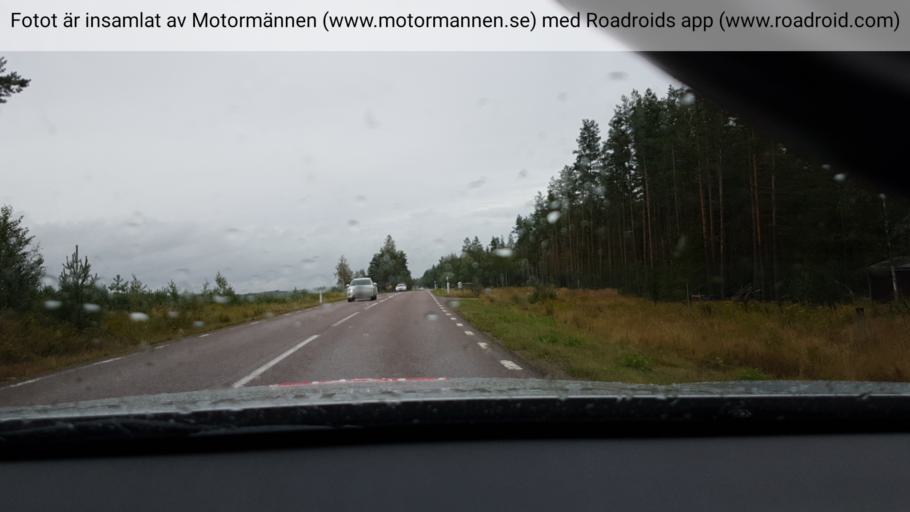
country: SE
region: Gaevleborg
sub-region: Gavle Kommun
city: Valbo
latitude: 60.5826
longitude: 16.9671
